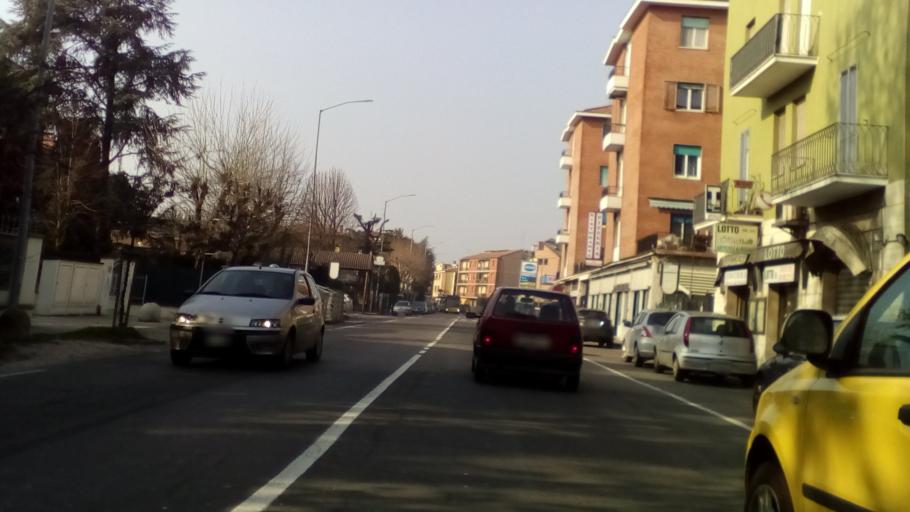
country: IT
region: Emilia-Romagna
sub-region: Provincia di Modena
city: Modena
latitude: 44.6307
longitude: 10.9415
